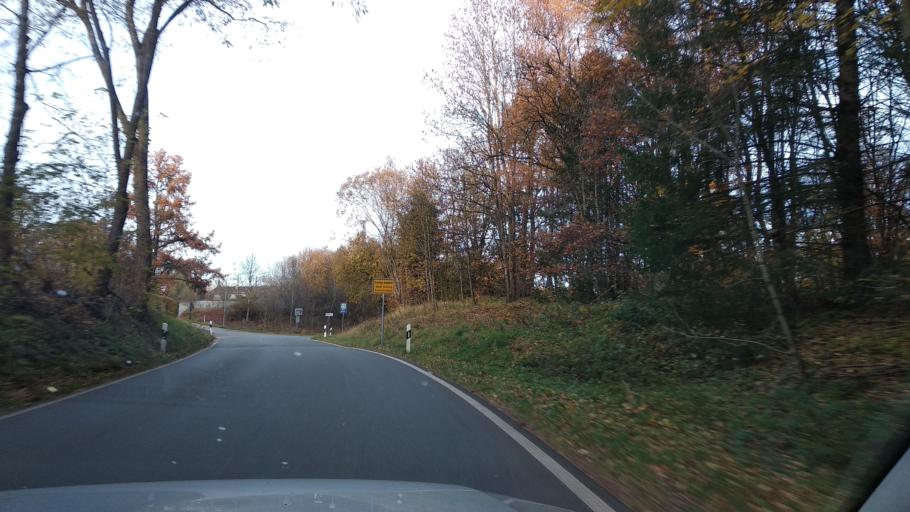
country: DE
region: Bavaria
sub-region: Upper Bavaria
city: Grafing bei Munchen
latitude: 48.0399
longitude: 11.9411
